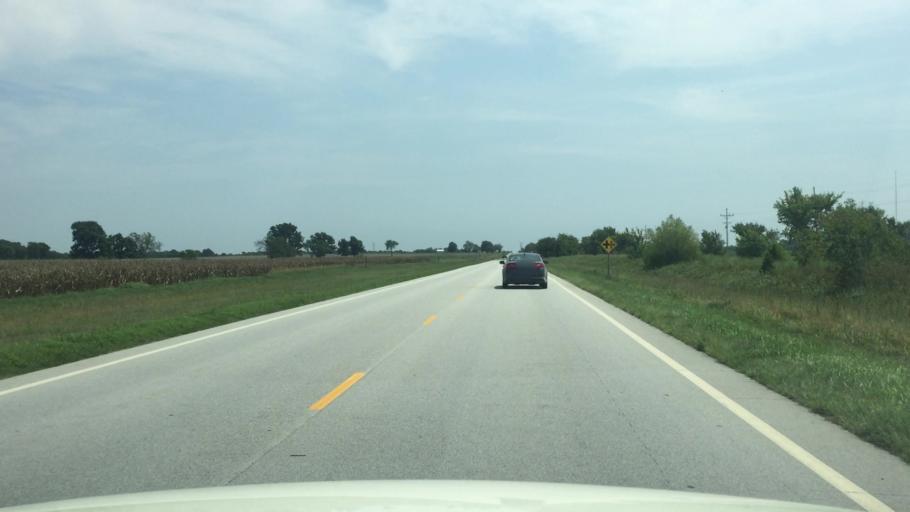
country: US
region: Kansas
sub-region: Cherokee County
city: Columbus
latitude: 37.1792
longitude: -94.9257
